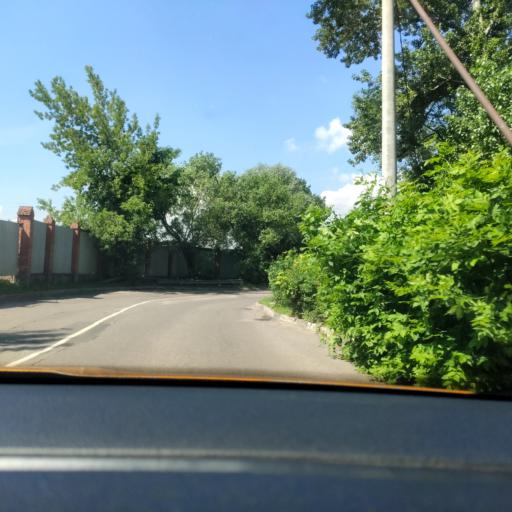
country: RU
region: Moskovskaya
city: Reutov
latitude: 55.7506
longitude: 37.8482
